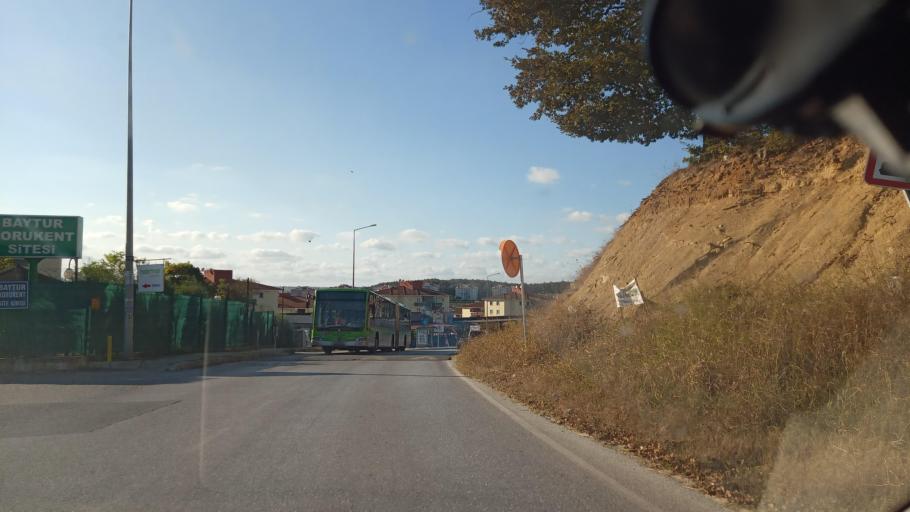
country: TR
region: Sakarya
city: Kazimpasa
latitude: 40.8547
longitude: 30.2779
